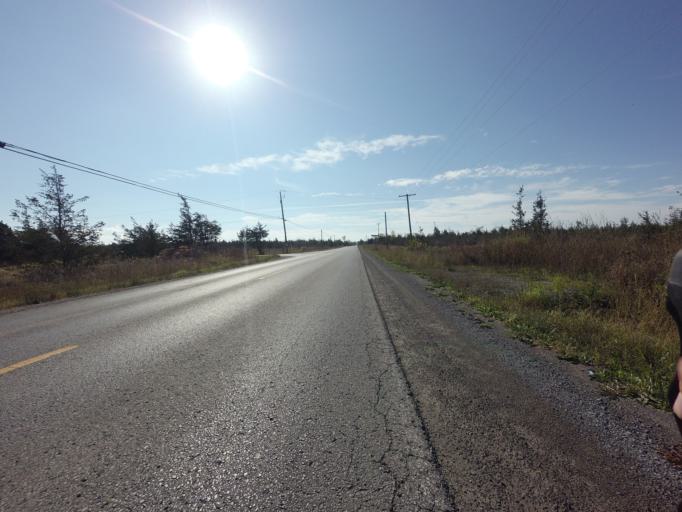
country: CA
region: Ontario
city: Prince Edward
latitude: 44.0231
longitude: -77.3660
